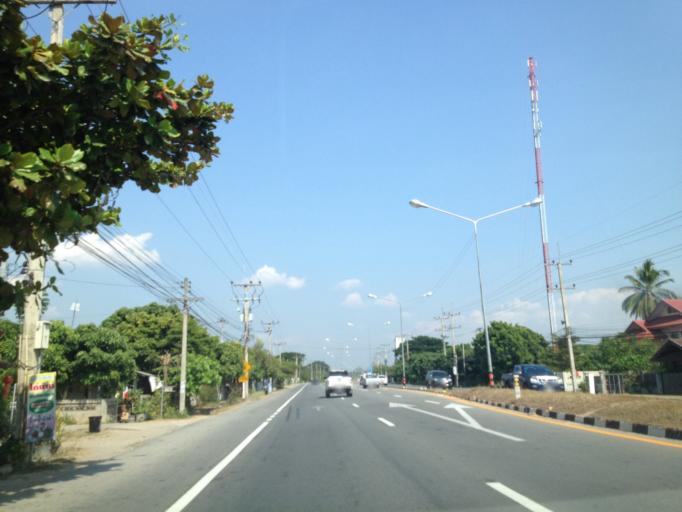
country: TH
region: Chiang Mai
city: Doi Lo
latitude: 18.5018
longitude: 98.8222
